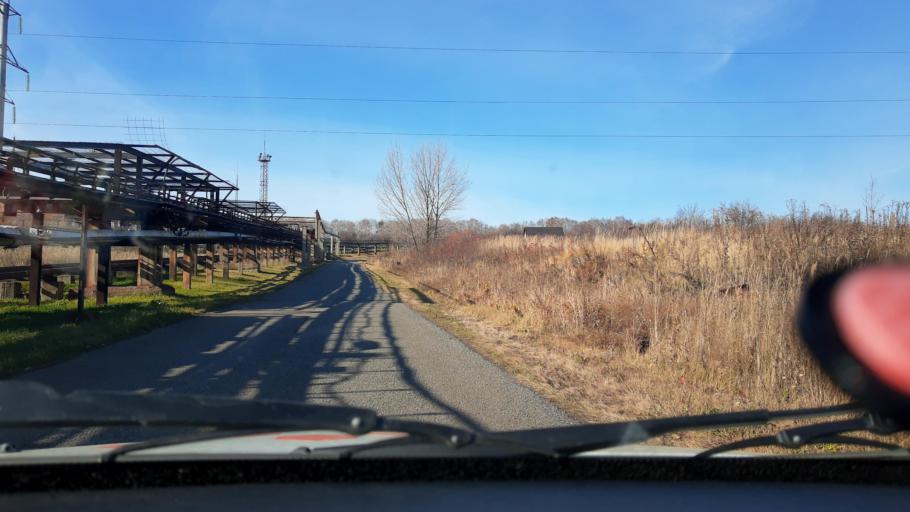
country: RU
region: Bashkortostan
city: Blagoveshchensk
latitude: 54.8878
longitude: 56.1018
